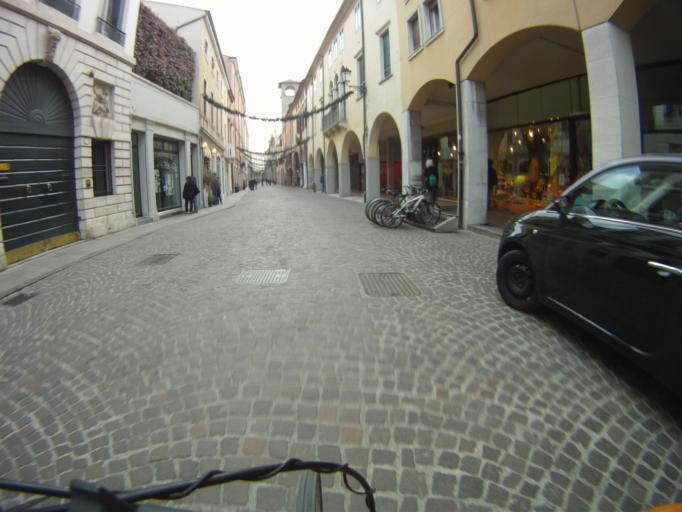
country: IT
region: Veneto
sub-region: Provincia di Padova
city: Padova
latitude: 45.4027
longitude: 11.8755
